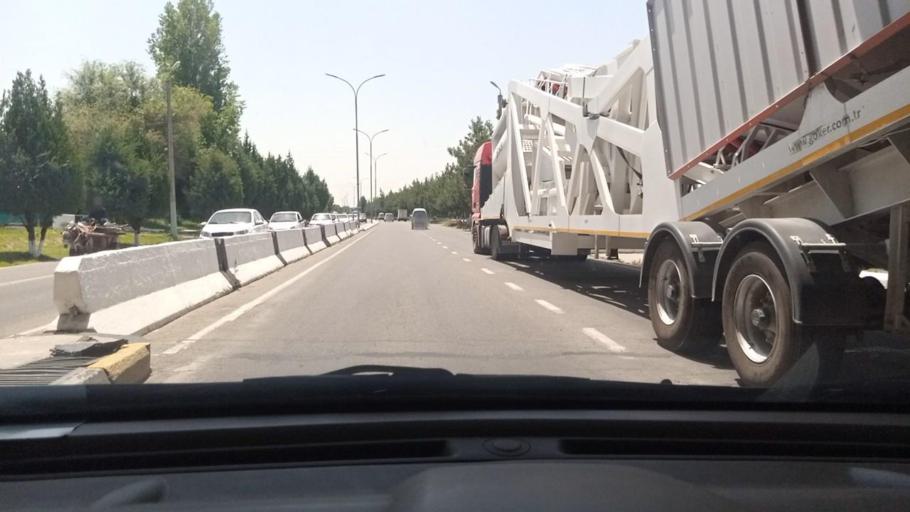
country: UZ
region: Toshkent
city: Urtaowul
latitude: 41.2149
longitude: 69.1728
